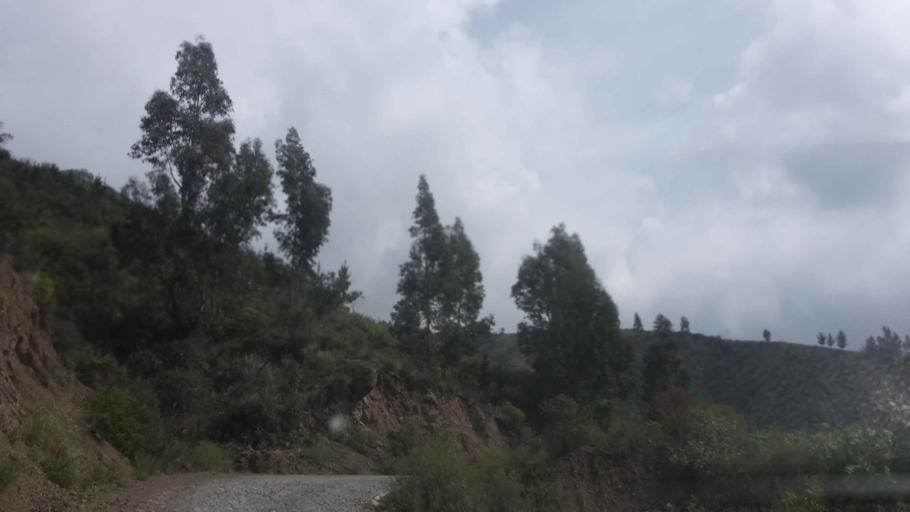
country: BO
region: Cochabamba
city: Cochabamba
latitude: -17.3625
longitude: -66.0519
